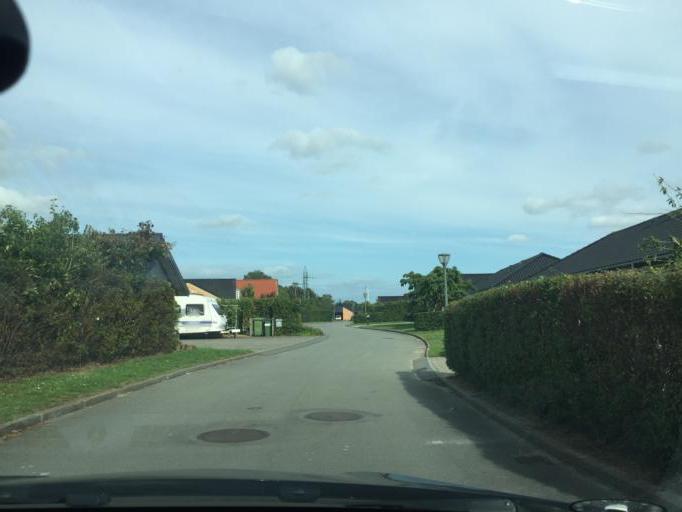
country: DK
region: South Denmark
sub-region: Odense Kommune
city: Neder Holluf
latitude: 55.3572
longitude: 10.5102
